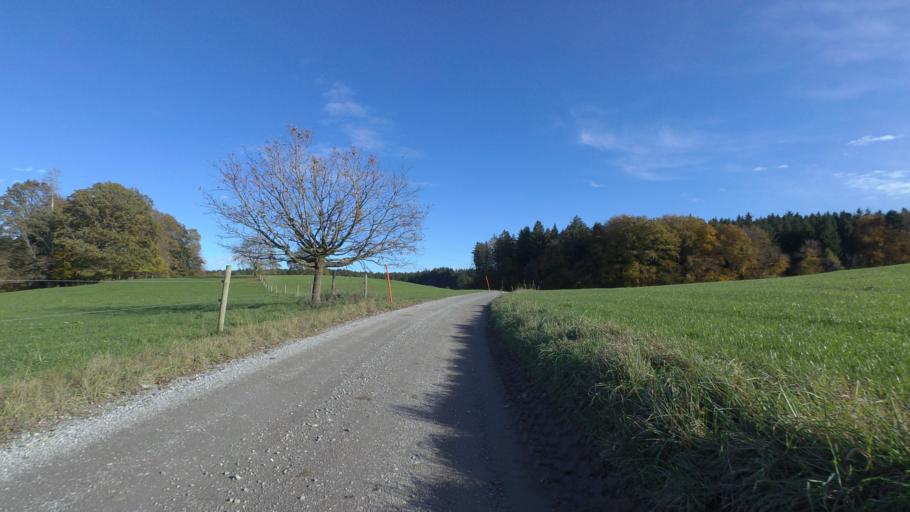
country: DE
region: Bavaria
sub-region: Upper Bavaria
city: Nussdorf
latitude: 47.9190
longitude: 12.5718
